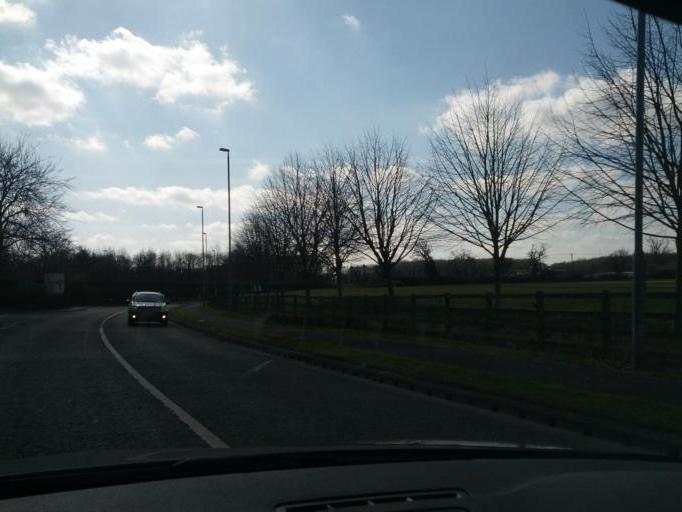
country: IE
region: Leinster
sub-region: Kildare
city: Leixlip
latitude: 53.3505
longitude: -6.5106
